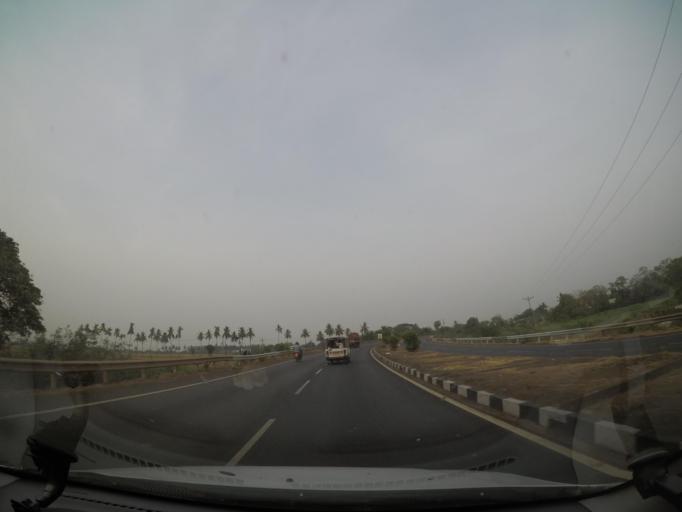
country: IN
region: Andhra Pradesh
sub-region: Krishna
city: Gannavaram
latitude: 16.6113
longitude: 80.9227
